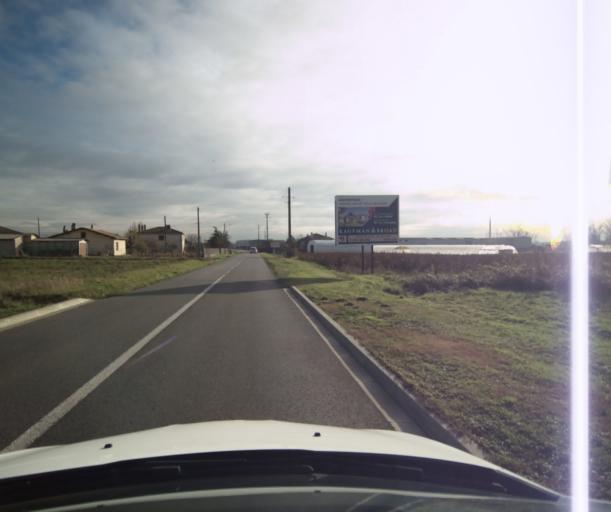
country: FR
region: Midi-Pyrenees
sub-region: Departement de la Haute-Garonne
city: Bruguieres
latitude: 43.7188
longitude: 1.4163
